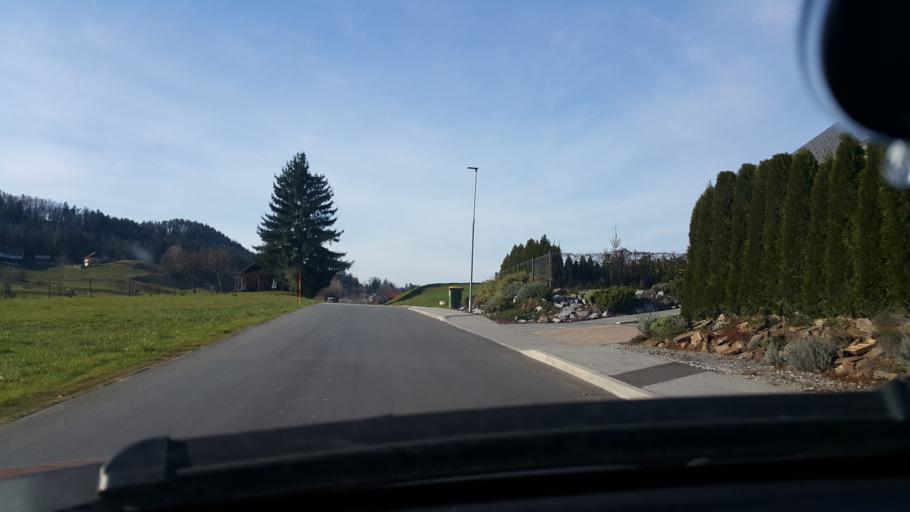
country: SI
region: Dobrna
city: Dobrna
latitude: 46.3434
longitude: 15.1689
